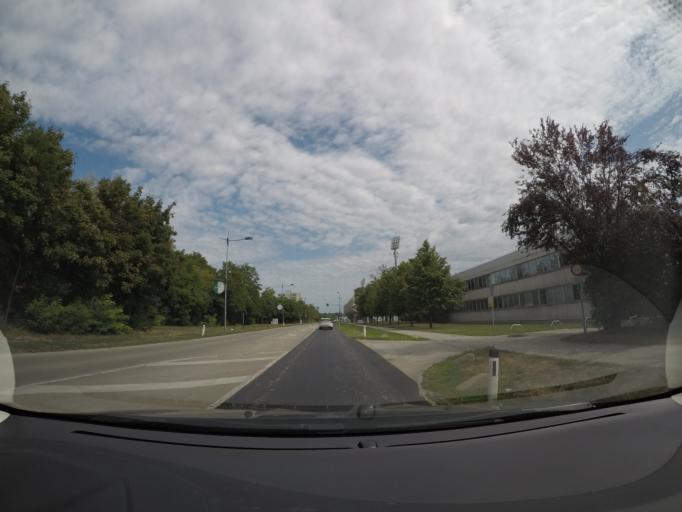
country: AT
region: Lower Austria
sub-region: Politischer Bezirk Modling
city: Wiener Neudorf
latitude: 48.0959
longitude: 16.3098
